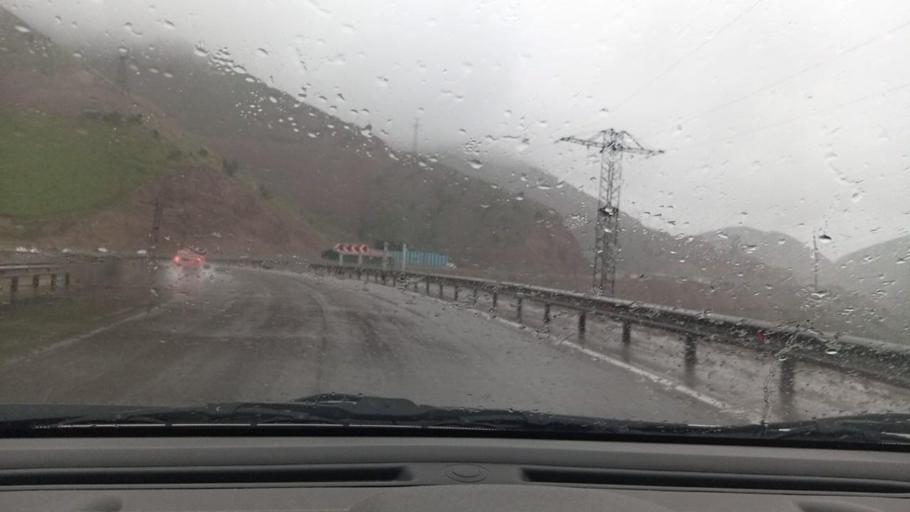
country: UZ
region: Toshkent
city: Angren
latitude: 41.0939
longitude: 70.5265
